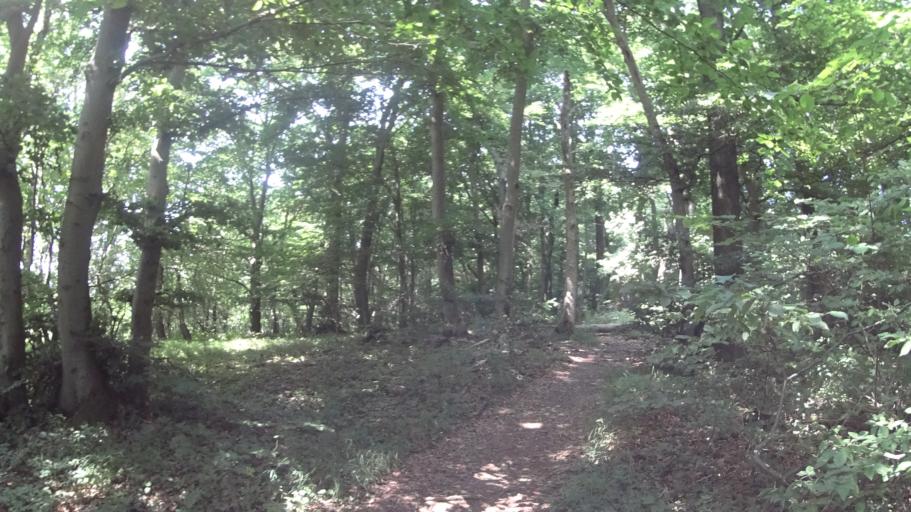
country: DE
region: Lower Saxony
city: Elbe
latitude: 52.0716
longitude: 10.3530
